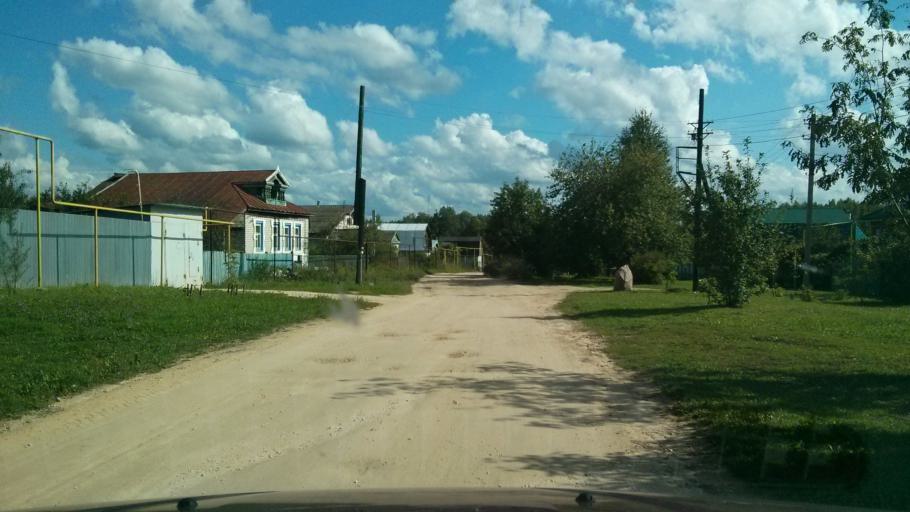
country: RU
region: Nizjnij Novgorod
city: Vacha
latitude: 55.7582
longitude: 42.5168
